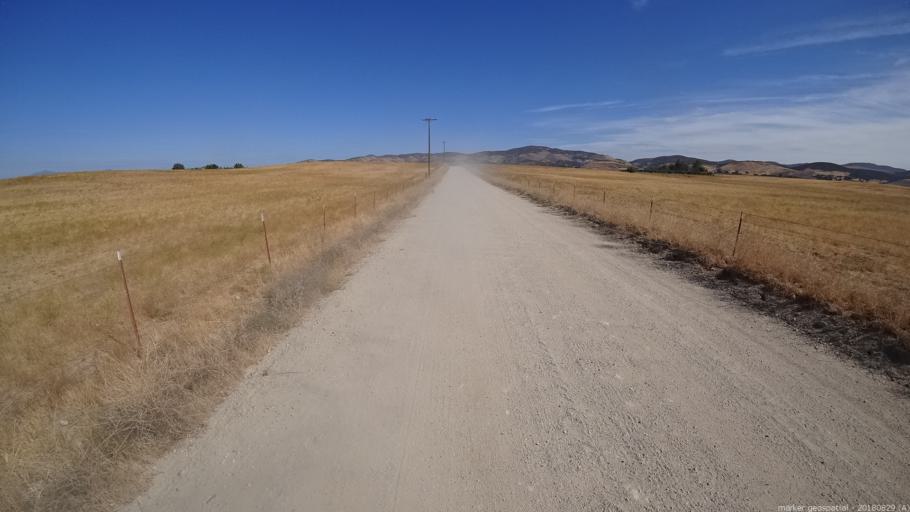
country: US
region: California
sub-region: Monterey County
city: King City
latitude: 35.9534
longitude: -121.0999
